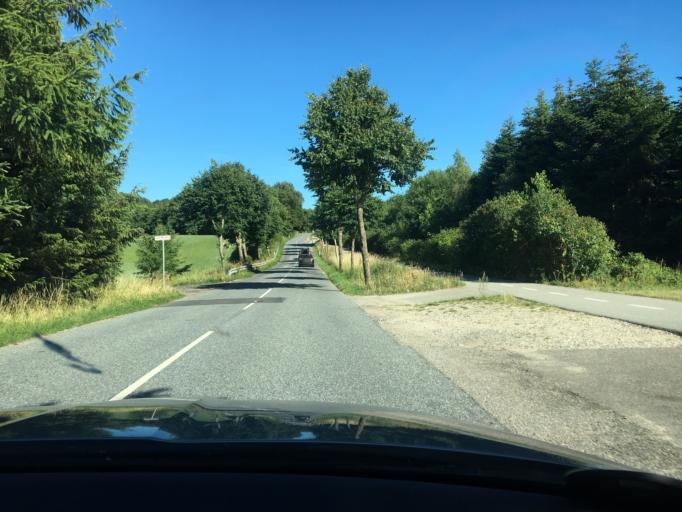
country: DK
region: Central Jutland
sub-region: Syddjurs Kommune
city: Hornslet
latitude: 56.3115
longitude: 10.3349
